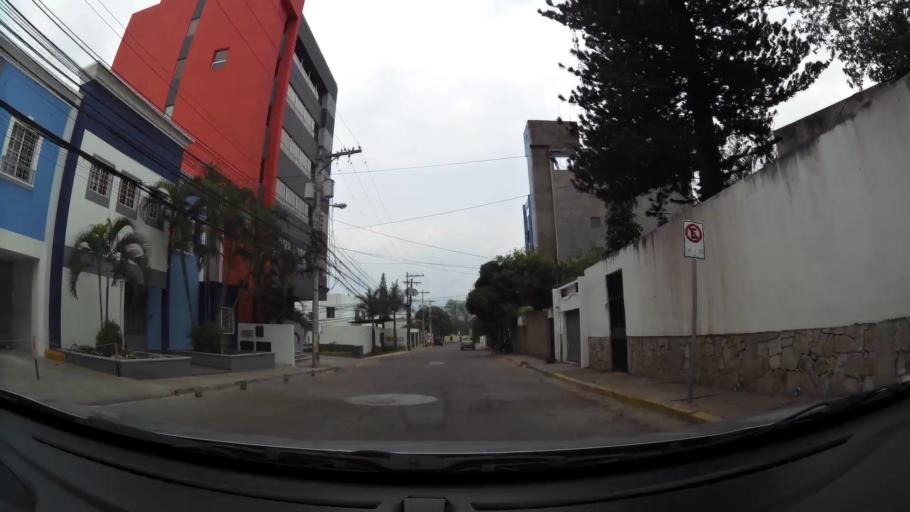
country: HN
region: Francisco Morazan
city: Tegucigalpa
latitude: 14.1008
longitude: -87.1917
